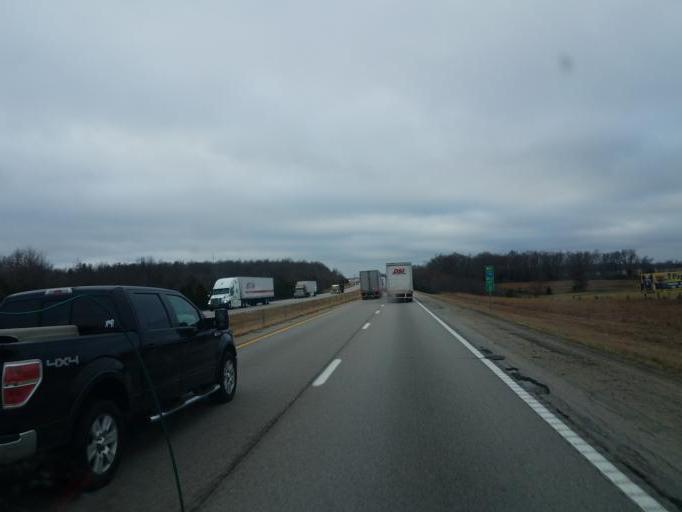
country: US
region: Missouri
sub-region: Laclede County
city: Lebanon
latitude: 37.5495
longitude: -92.8060
